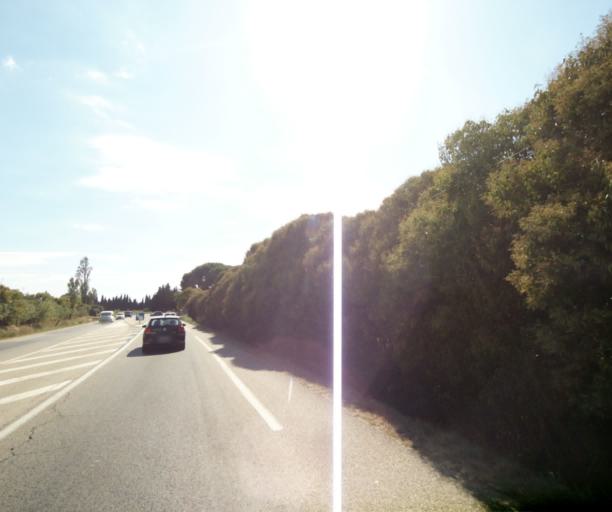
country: FR
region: Languedoc-Roussillon
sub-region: Departement du Gard
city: Caissargues
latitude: 43.8029
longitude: 4.4032
